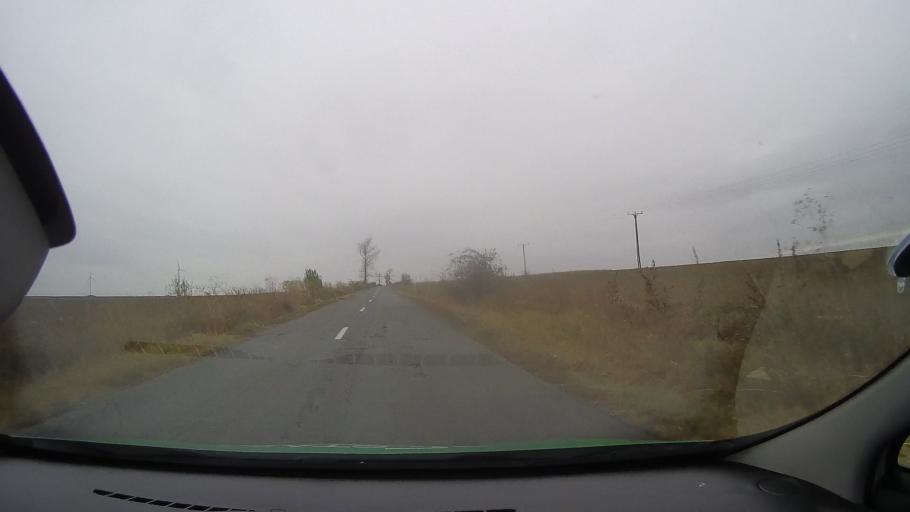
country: RO
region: Constanta
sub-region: Comuna Pantelimon
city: Pantelimon
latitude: 44.5614
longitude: 28.3213
